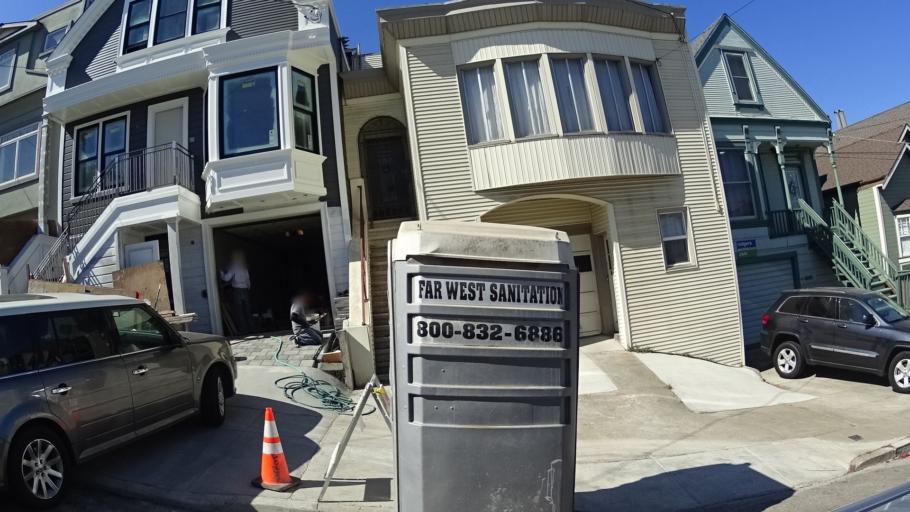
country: US
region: California
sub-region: San Francisco County
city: San Francisco
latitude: 37.7503
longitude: -122.4395
